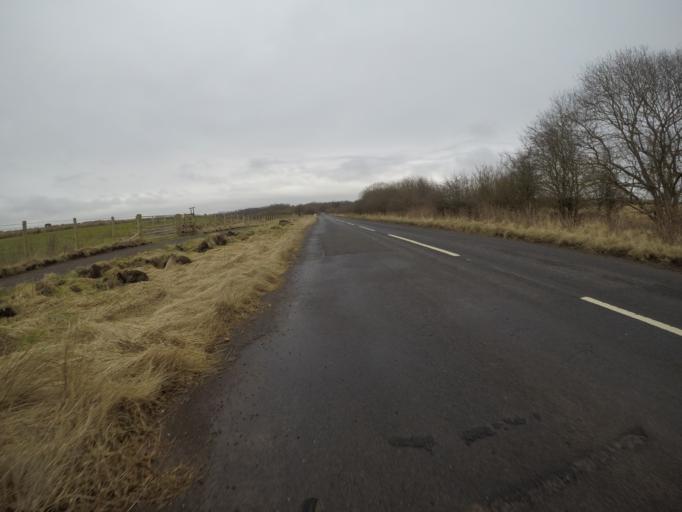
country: GB
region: Scotland
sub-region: North Ayrshire
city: Kilwinning
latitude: 55.6364
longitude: -4.6908
